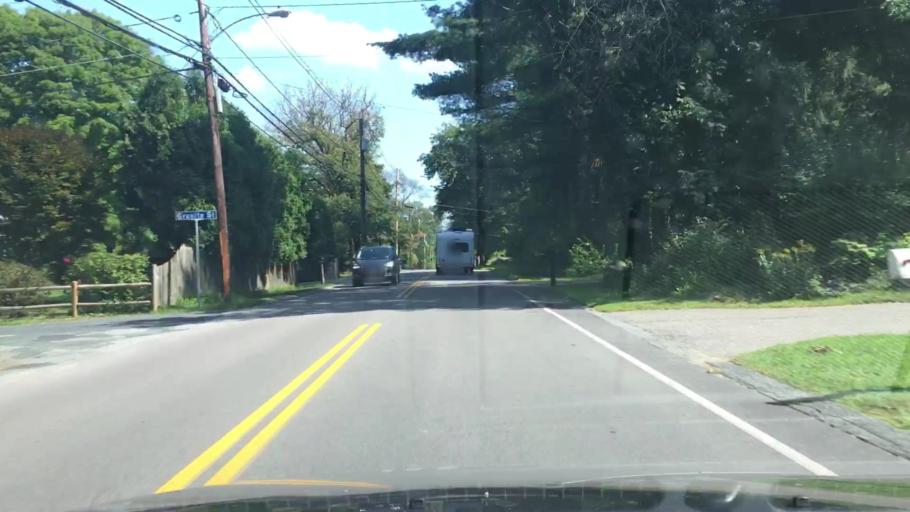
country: US
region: Massachusetts
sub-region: Middlesex County
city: Holliston
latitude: 42.2007
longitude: -71.4127
